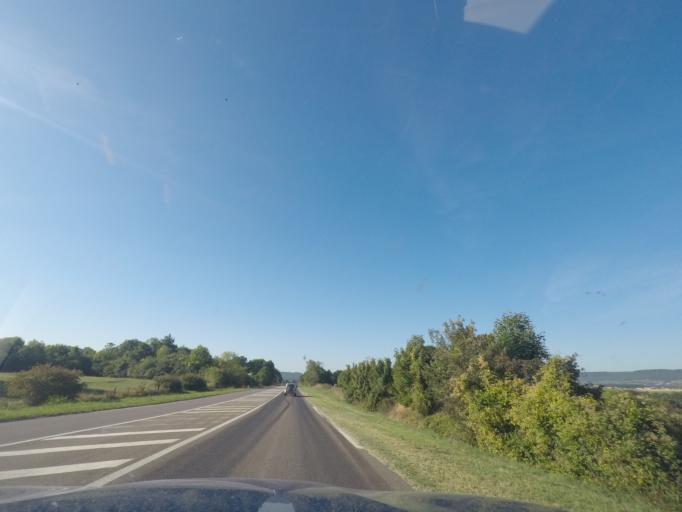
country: FR
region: Lorraine
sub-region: Departement de la Moselle
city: Hettange-Grande
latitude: 49.4230
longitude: 6.1623
